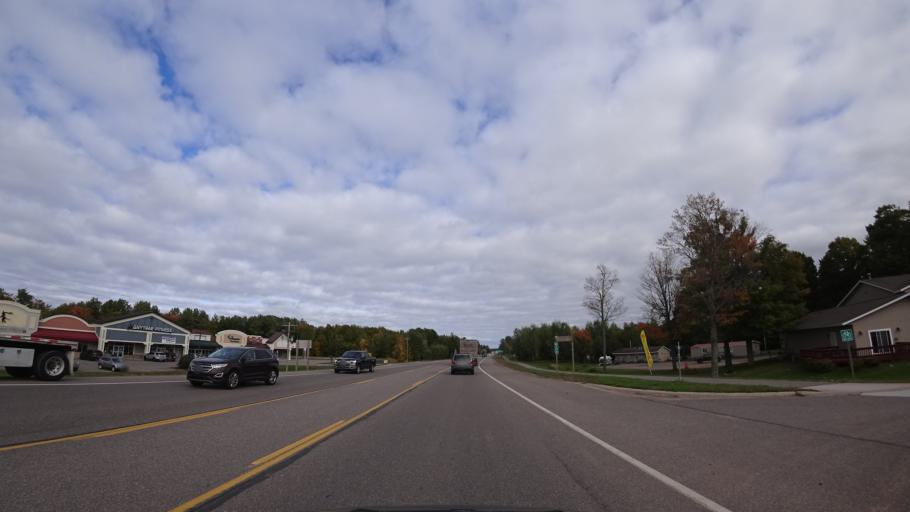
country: US
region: Michigan
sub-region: Marquette County
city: Harvey
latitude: 46.4871
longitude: -87.3486
